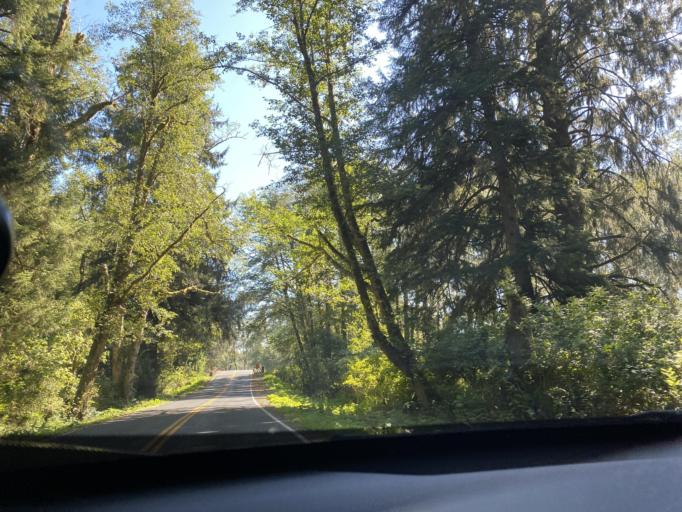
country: US
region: Washington
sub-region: Clallam County
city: Forks
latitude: 47.9223
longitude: -124.6216
